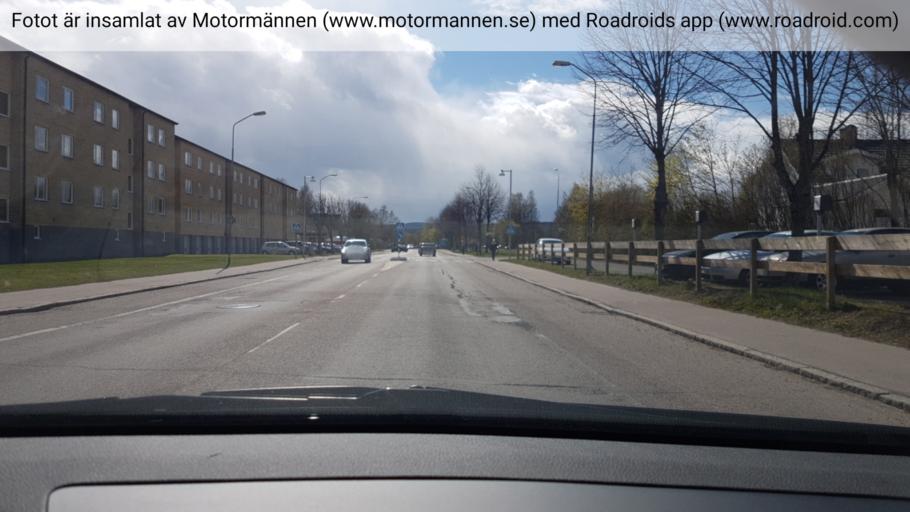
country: SE
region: Dalarna
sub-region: Borlange Kommun
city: Borlaenge
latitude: 60.4895
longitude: 15.4192
